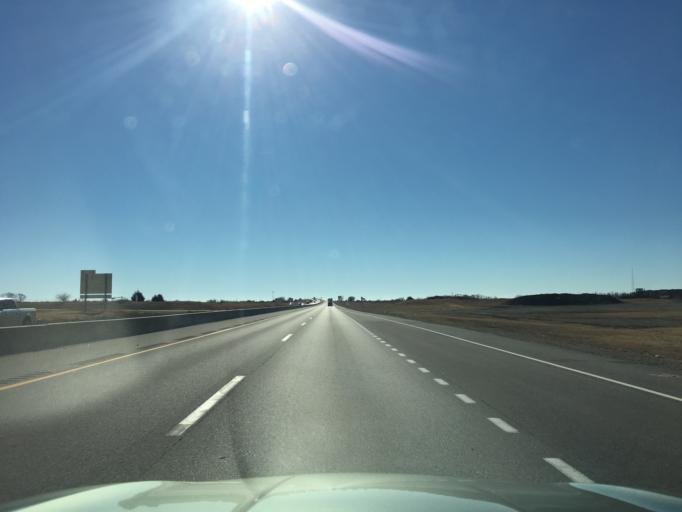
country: US
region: Kansas
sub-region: Sumner County
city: Wellington
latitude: 37.2761
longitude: -97.3404
